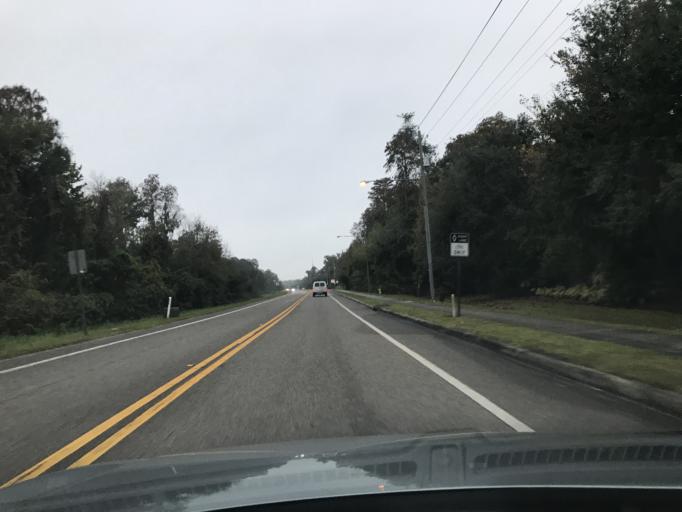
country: US
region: Florida
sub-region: Hillsborough County
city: Westchase
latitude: 28.0561
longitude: -82.6295
